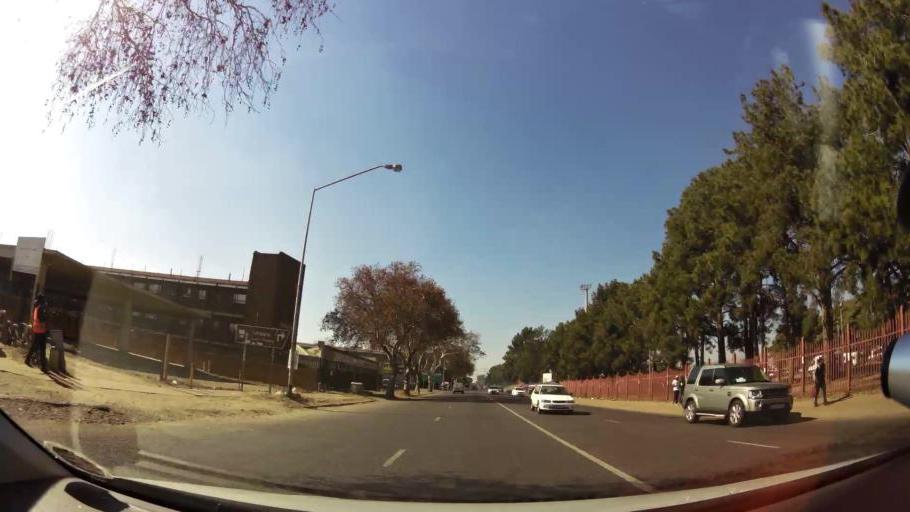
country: ZA
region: Gauteng
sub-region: City of Tshwane Metropolitan Municipality
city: Pretoria
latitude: -25.7477
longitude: 28.1689
